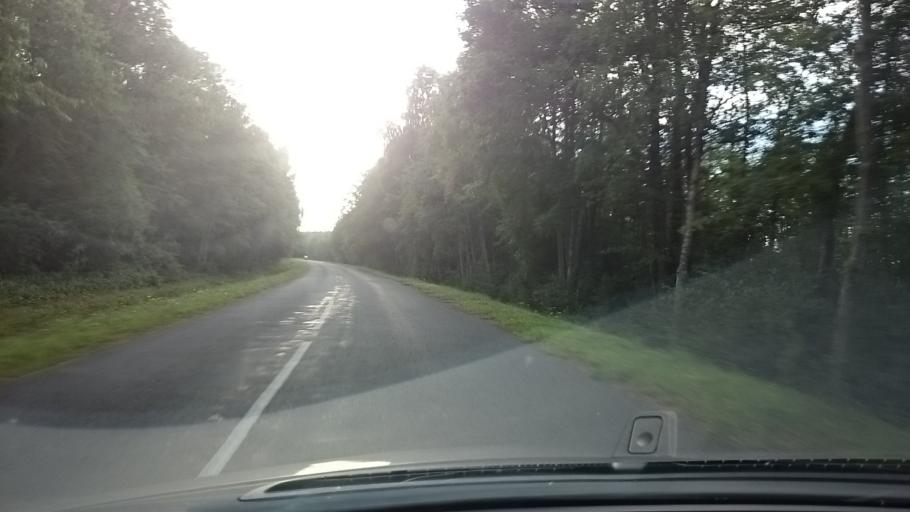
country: EE
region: Saare
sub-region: Kuressaare linn
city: Kuressaare
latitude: 58.4155
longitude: 22.0882
